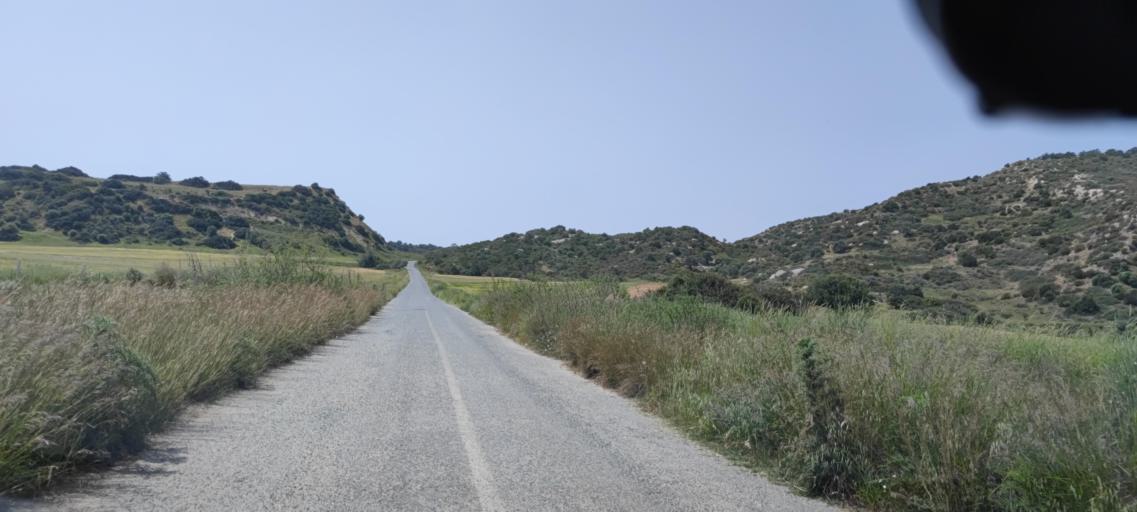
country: CY
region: Ammochostos
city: Rizokarpaso
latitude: 35.5301
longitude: 34.3291
